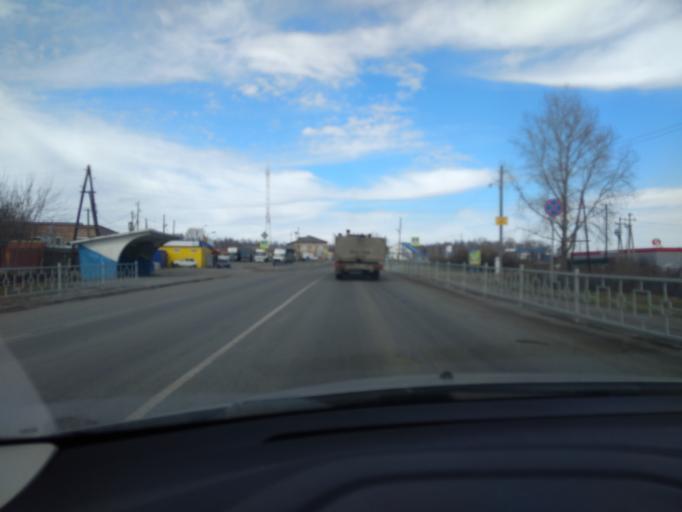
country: RU
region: Sverdlovsk
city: Pyshma
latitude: 56.9501
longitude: 63.2256
